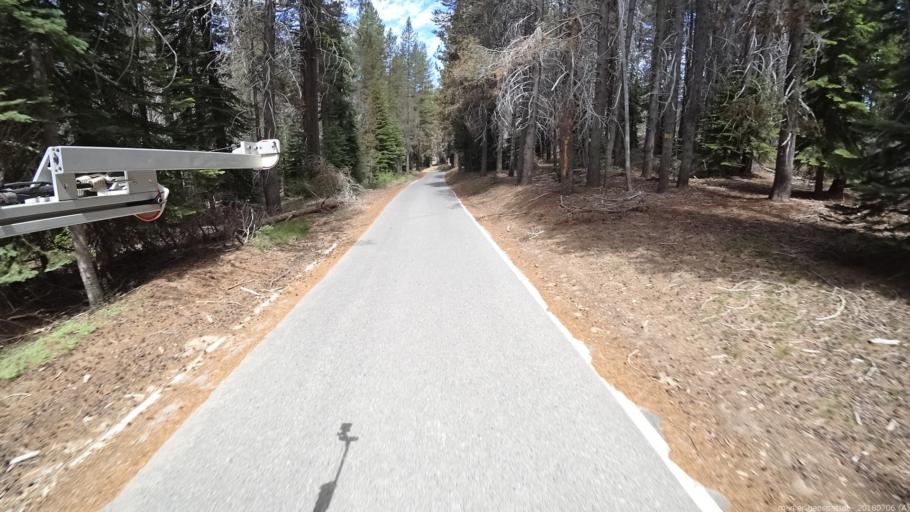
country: US
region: California
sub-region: Madera County
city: Oakhurst
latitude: 37.4469
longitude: -119.4502
